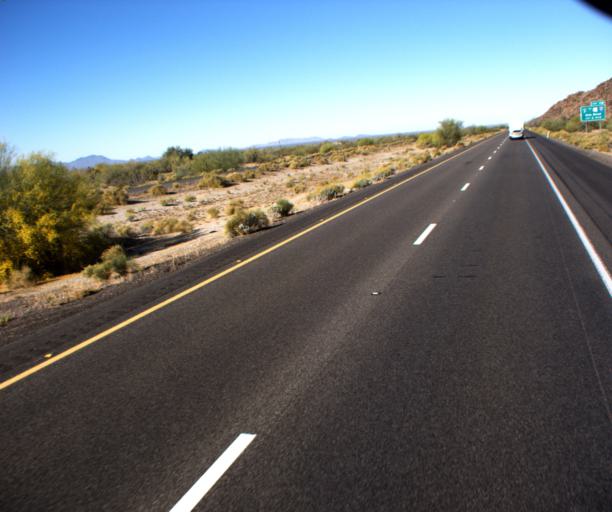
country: US
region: Arizona
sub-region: Maricopa County
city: Gila Bend
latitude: 32.9066
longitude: -112.5624
